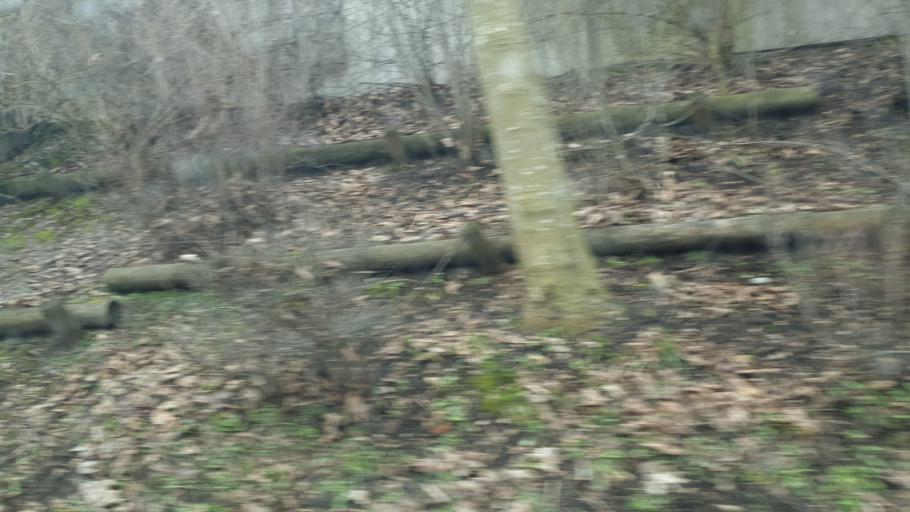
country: DE
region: Bavaria
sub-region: Upper Bavaria
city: Grobenzell
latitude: 48.1797
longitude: 11.3821
